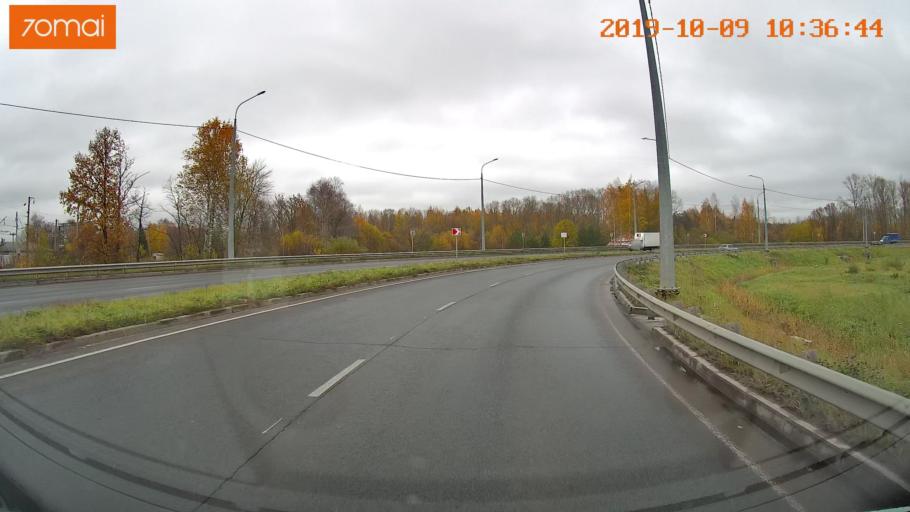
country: RU
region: Vologda
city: Vologda
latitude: 59.2347
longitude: 39.8677
